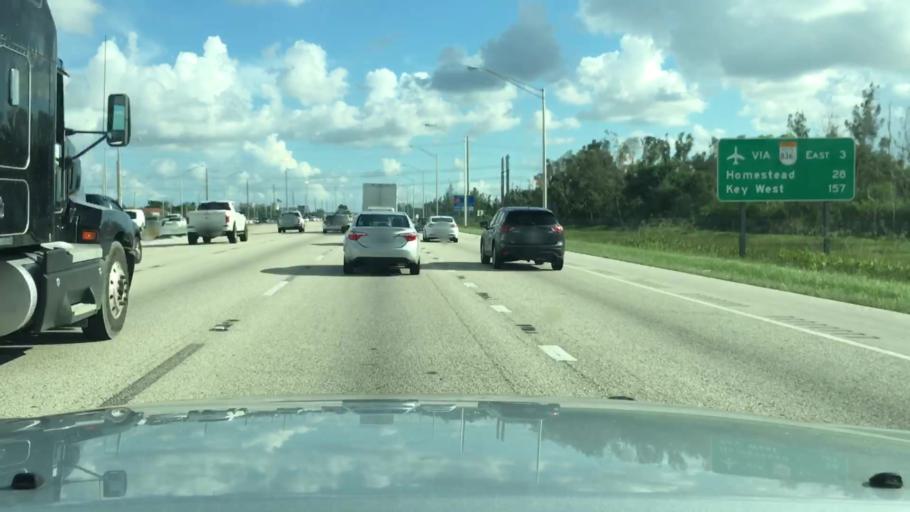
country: US
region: Florida
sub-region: Miami-Dade County
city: Doral
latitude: 25.8218
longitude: -80.3873
